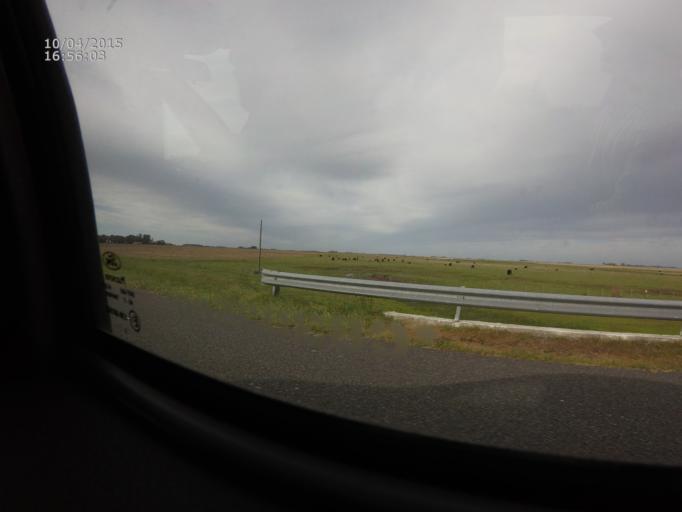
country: AR
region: Buenos Aires
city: Coronel Vidal
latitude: -37.5324
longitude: -57.7052
